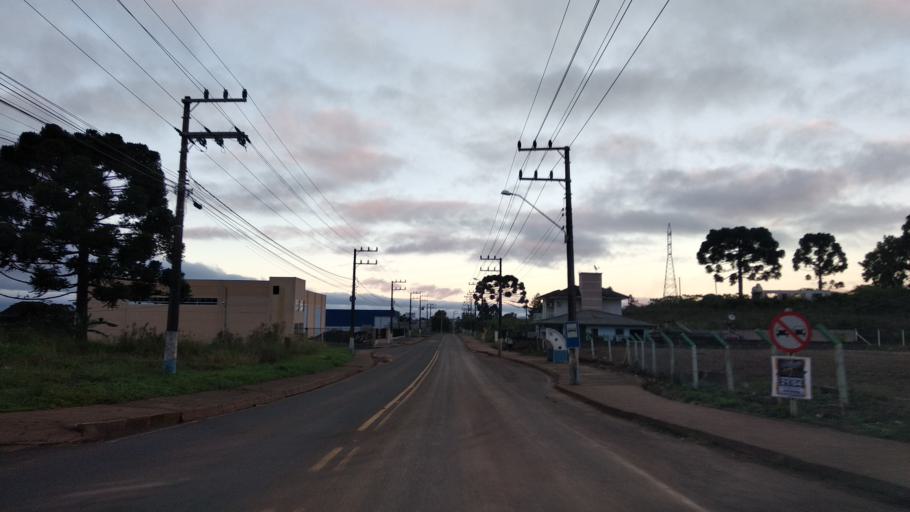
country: BR
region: Santa Catarina
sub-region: Campos Novos
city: Campos Novos
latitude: -27.3807
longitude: -51.2094
